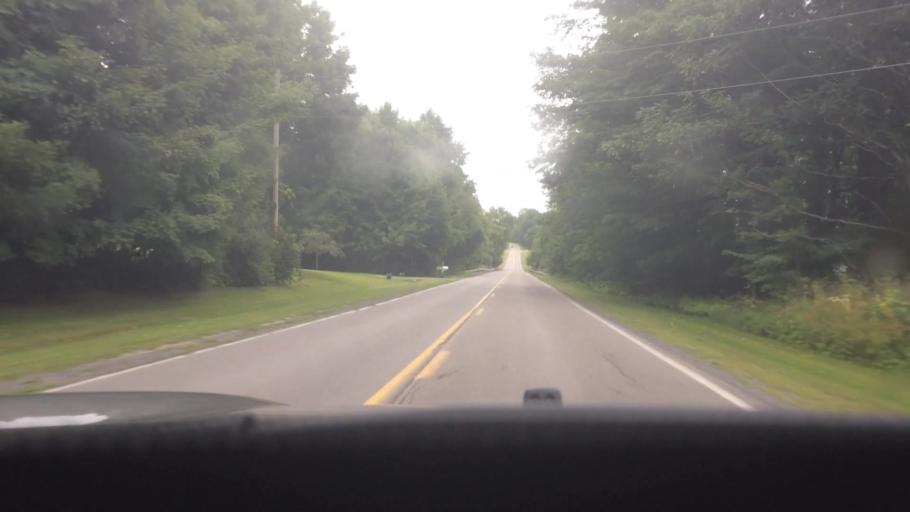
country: US
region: New York
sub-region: St. Lawrence County
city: Canton
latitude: 44.5386
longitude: -75.0748
